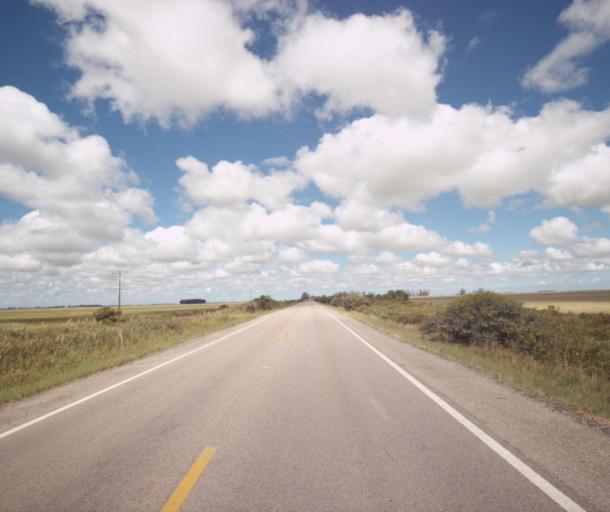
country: BR
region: Rio Grande do Sul
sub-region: Rio Grande
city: Rio Grande
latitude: -32.1734
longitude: -52.4154
